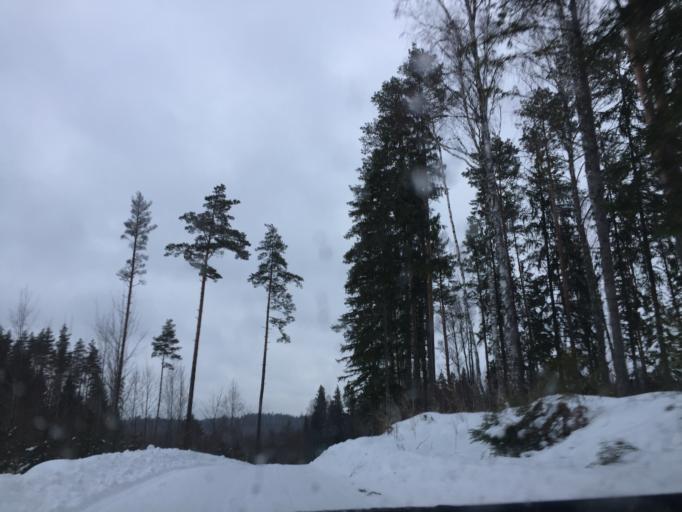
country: LV
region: Amatas Novads
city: Drabesi
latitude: 57.2026
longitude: 25.2974
